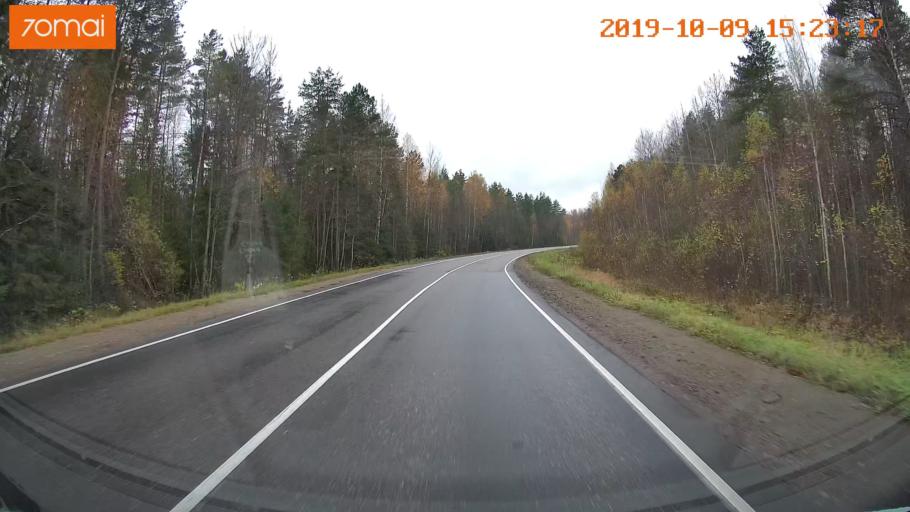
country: RU
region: Kostroma
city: Susanino
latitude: 58.0361
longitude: 41.4842
